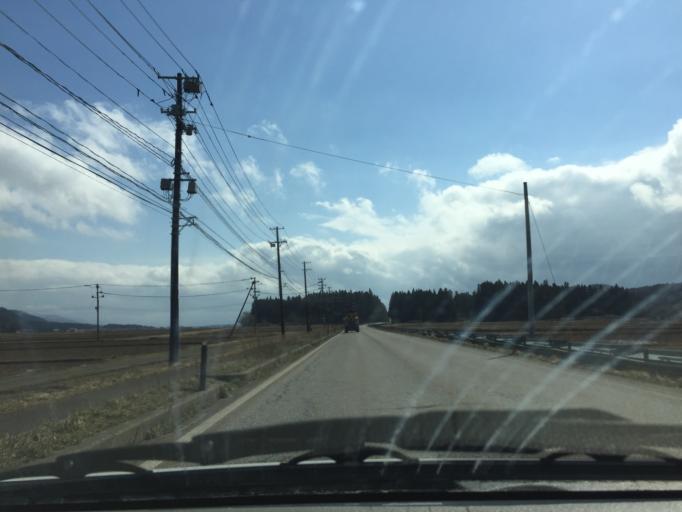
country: JP
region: Fukushima
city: Inawashiro
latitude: 37.5939
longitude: 140.1329
